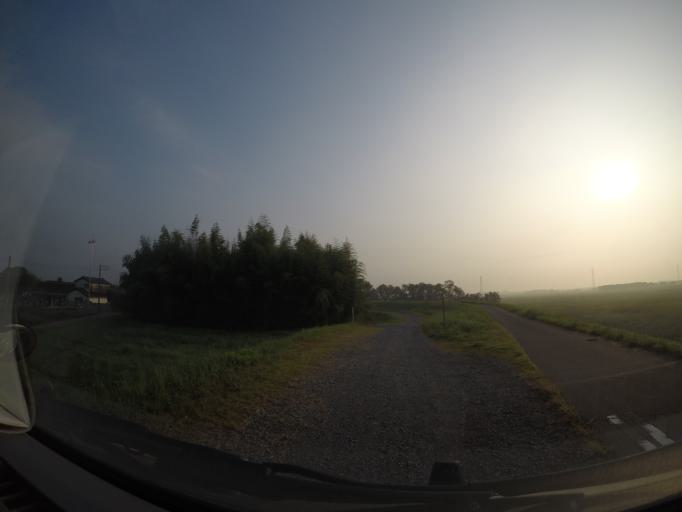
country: JP
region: Tochigi
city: Fujioka
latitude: 36.2637
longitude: 139.6792
